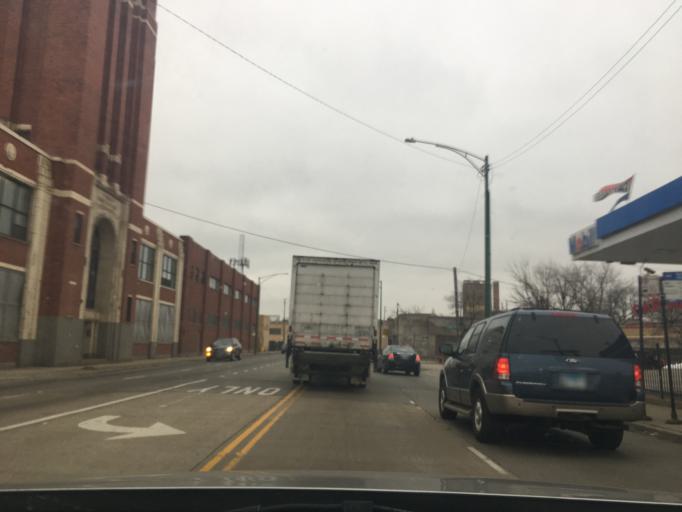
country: US
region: Illinois
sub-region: Cook County
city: Oak Park
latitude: 41.9020
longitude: -87.7460
